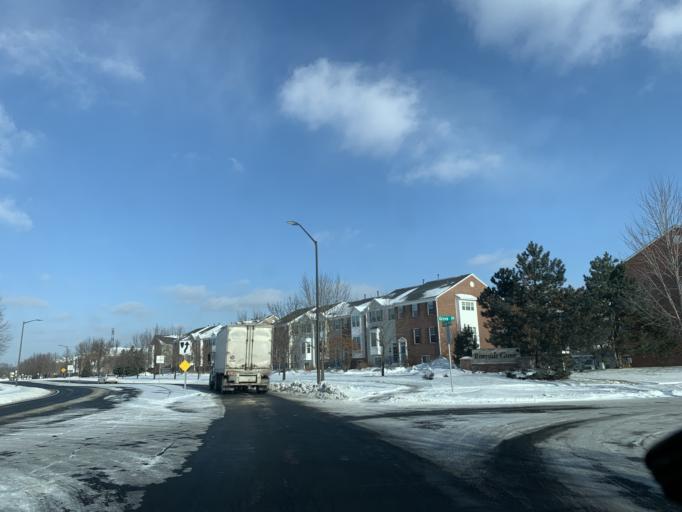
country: US
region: Minnesota
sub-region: Scott County
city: Prior Lake
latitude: 44.7724
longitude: -93.4104
